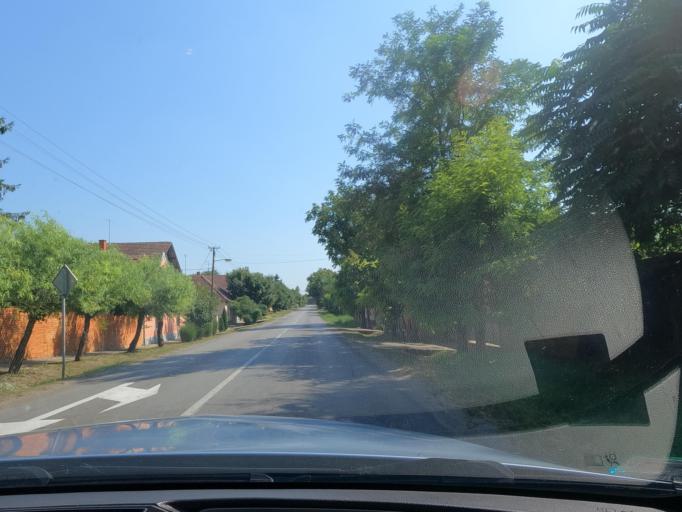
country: RS
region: Autonomna Pokrajina Vojvodina
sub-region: Severnobacki Okrug
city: Backa Topola
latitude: 45.8093
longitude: 19.6447
